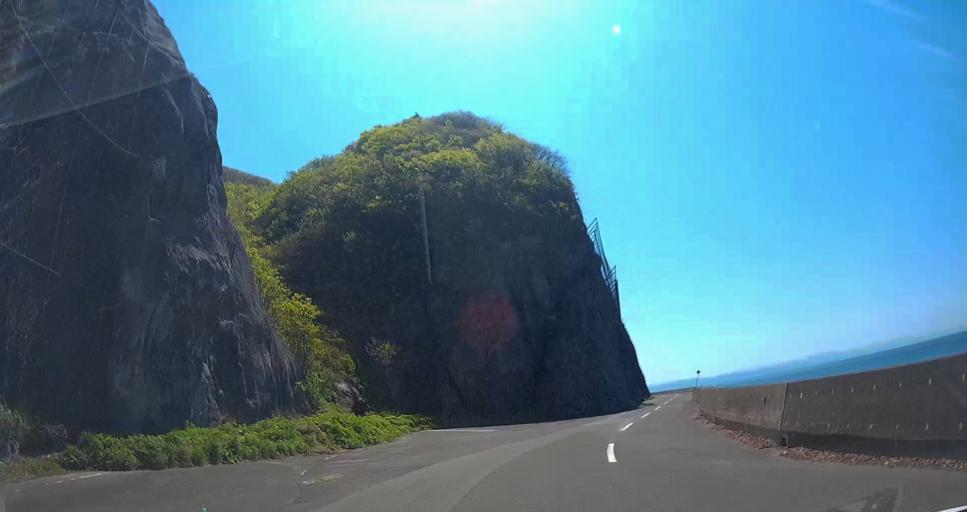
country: JP
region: Aomori
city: Aomori Shi
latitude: 41.1327
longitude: 140.7819
